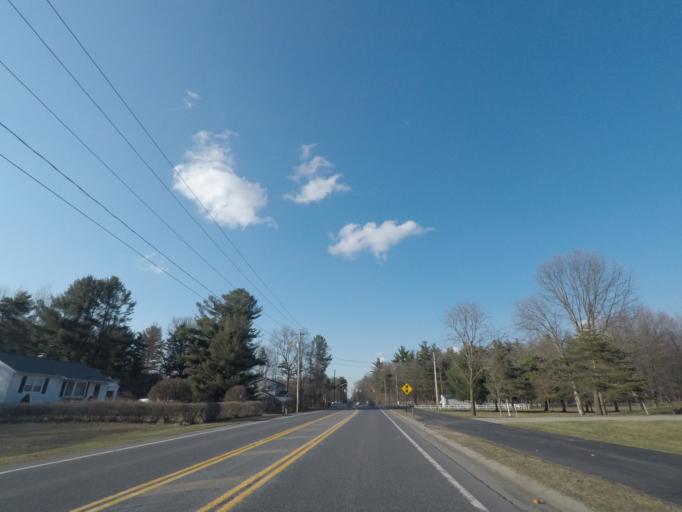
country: US
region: New York
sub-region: Saratoga County
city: Country Knolls
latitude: 42.8390
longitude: -73.7941
